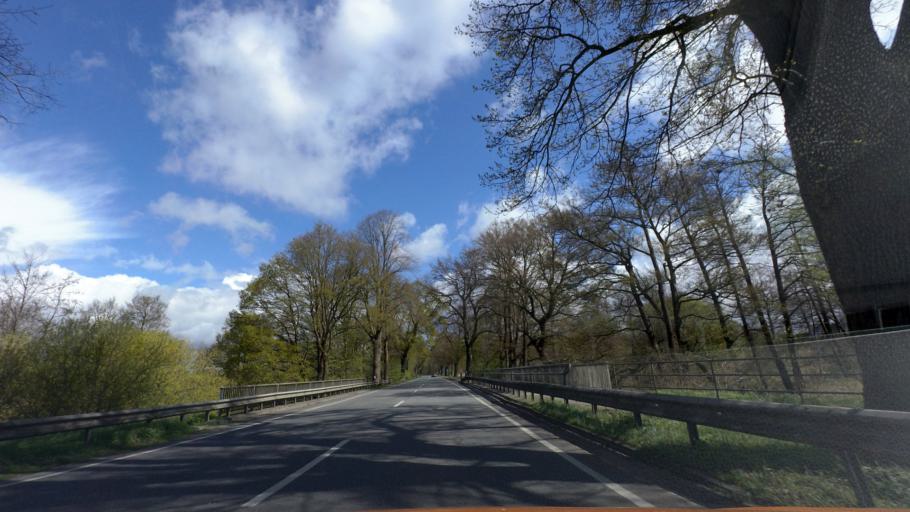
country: DE
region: Lower Saxony
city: Ottersberg
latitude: 53.1035
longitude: 9.1331
